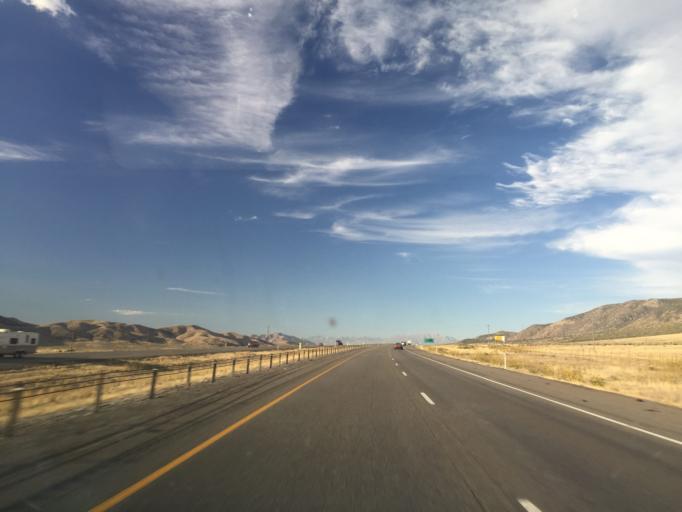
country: US
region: Utah
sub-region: Juab County
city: Mona
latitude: 39.8512
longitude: -111.8354
